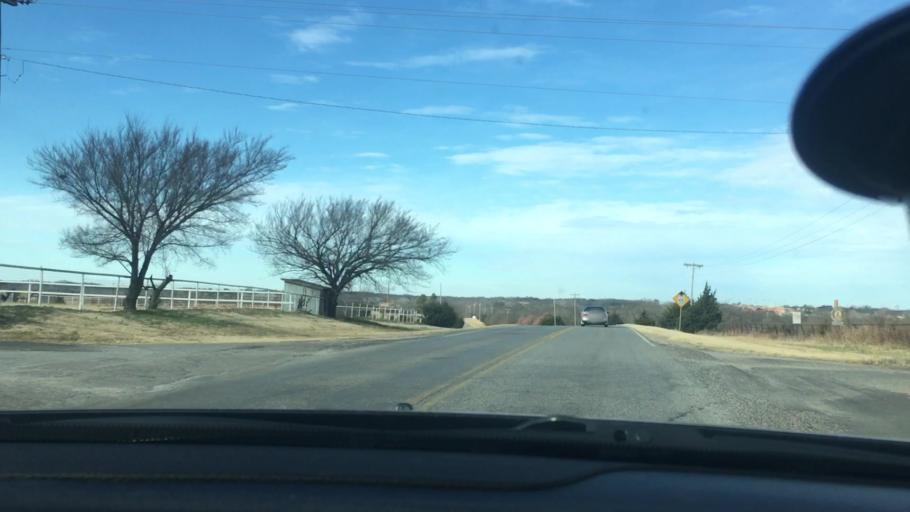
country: US
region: Oklahoma
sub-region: Seminole County
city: Konawa
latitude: 34.9489
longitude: -96.7399
